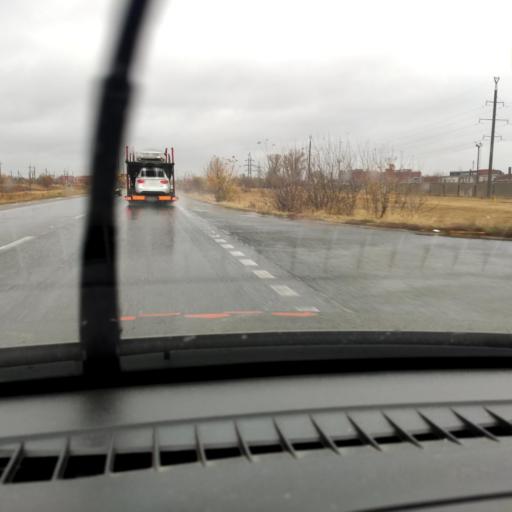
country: RU
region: Samara
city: Tol'yatti
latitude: 53.5707
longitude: 49.3450
